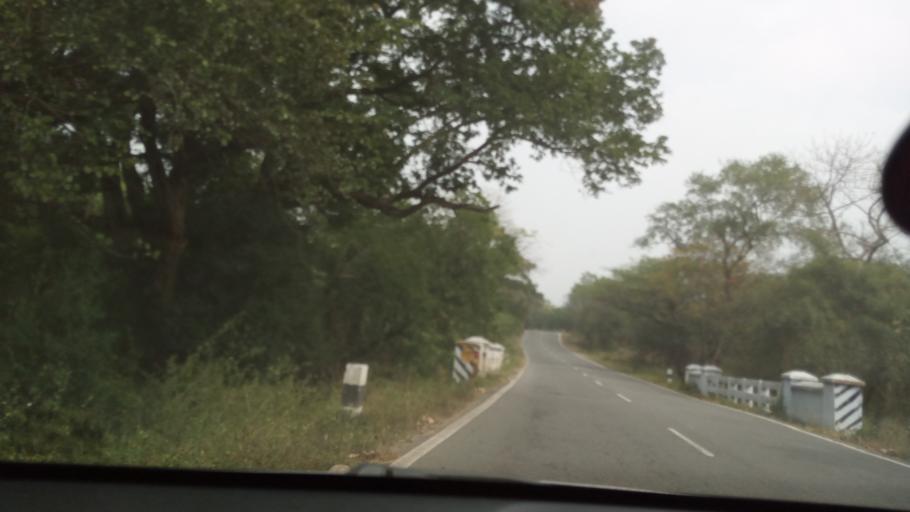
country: IN
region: Tamil Nadu
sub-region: Erode
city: Sathyamangalam
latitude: 11.5662
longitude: 77.1350
